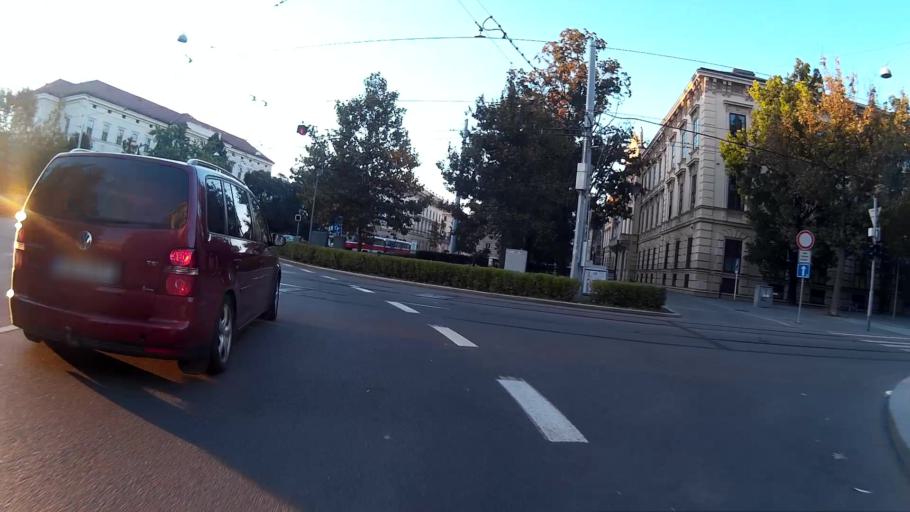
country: CZ
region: South Moravian
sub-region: Mesto Brno
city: Brno
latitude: 49.1973
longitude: 16.6027
